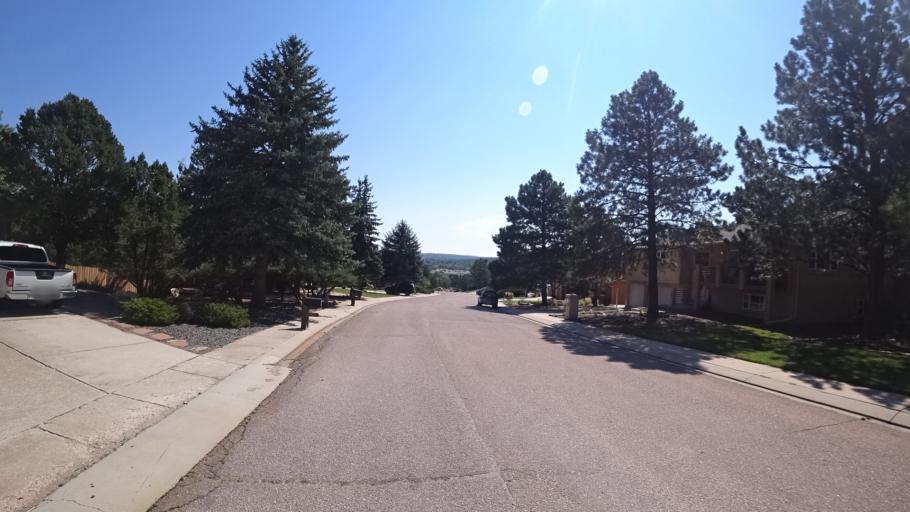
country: US
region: Colorado
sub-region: El Paso County
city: Air Force Academy
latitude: 38.9267
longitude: -104.8207
